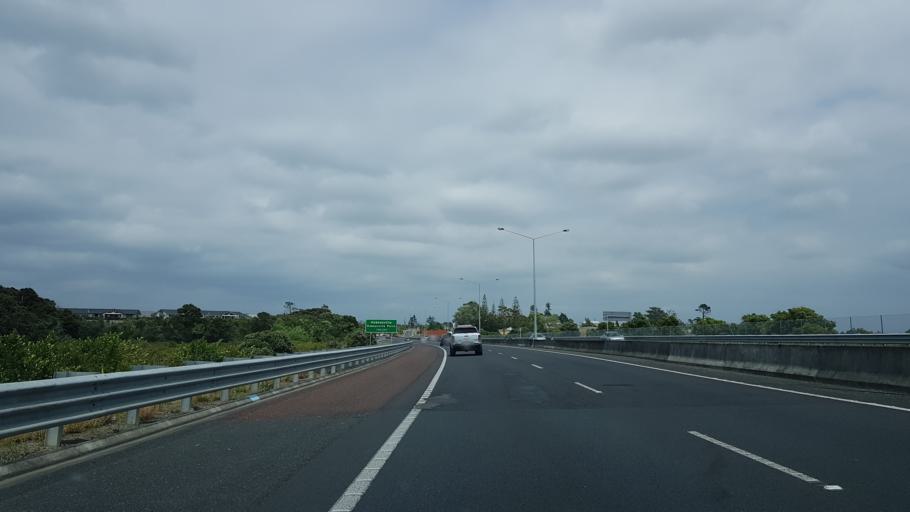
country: NZ
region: Auckland
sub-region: Auckland
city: North Shore
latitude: -36.7864
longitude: 174.6629
